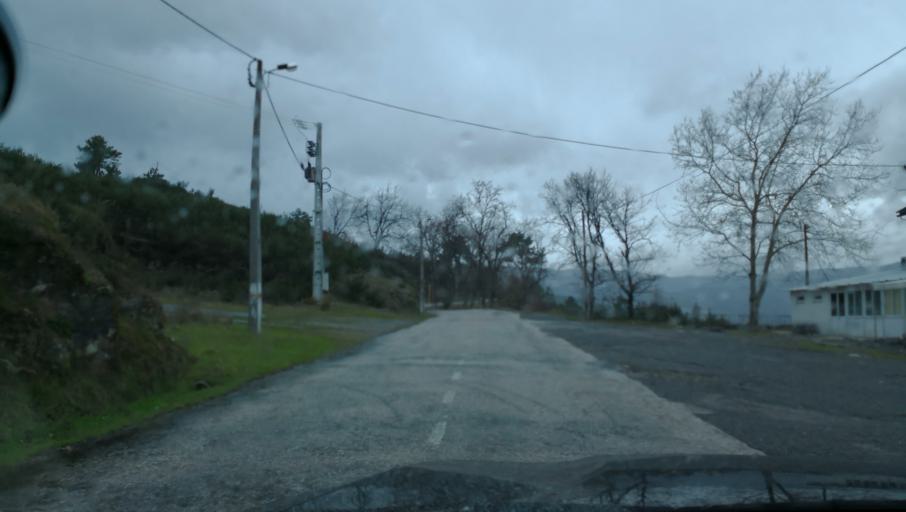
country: PT
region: Vila Real
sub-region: Vila Real
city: Vila Real
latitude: 41.2786
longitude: -7.7960
